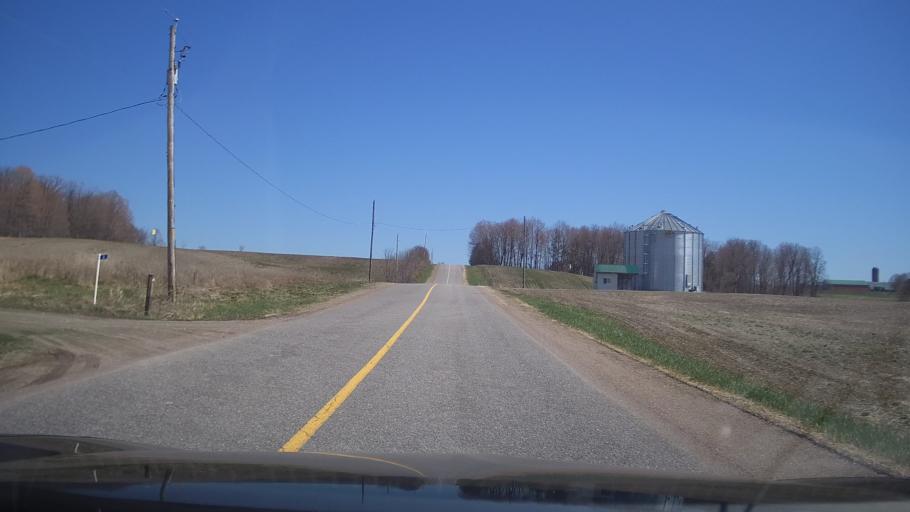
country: CA
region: Ontario
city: Arnprior
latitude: 45.5333
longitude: -76.3938
